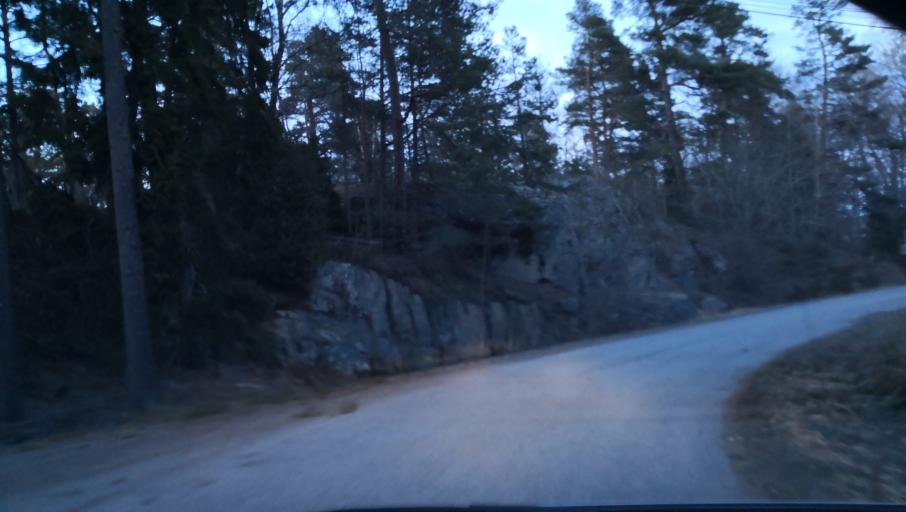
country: SE
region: Stockholm
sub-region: Varmdo Kommun
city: Gustavsberg
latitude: 59.3266
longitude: 18.3514
